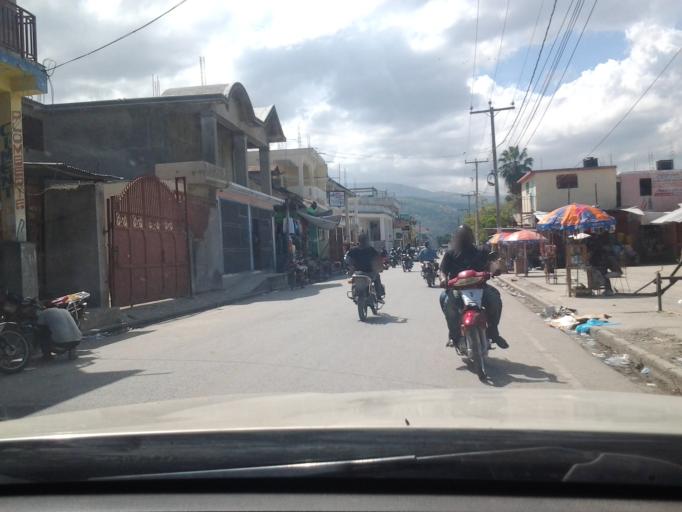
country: HT
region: Ouest
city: Tigwav
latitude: 18.4332
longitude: -72.8655
